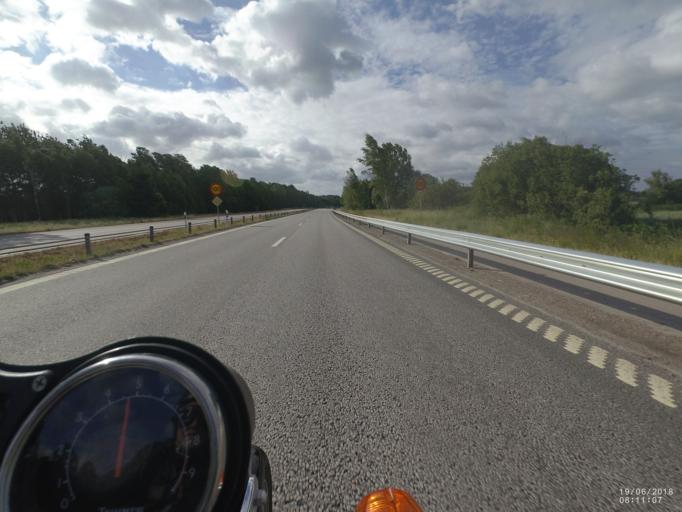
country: SE
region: Soedermanland
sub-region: Nykopings Kommun
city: Nykoping
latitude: 58.7425
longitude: 16.9985
